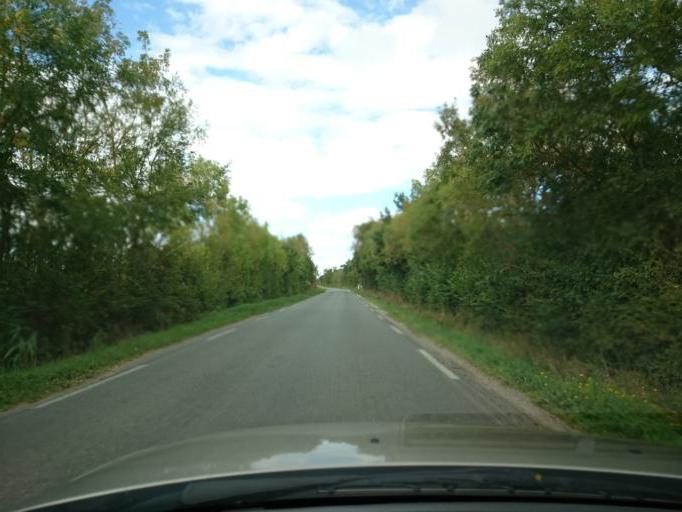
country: FR
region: Aquitaine
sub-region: Departement de la Gironde
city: Saint-Louis-de-Montferrand
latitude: 44.9698
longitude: -0.5549
